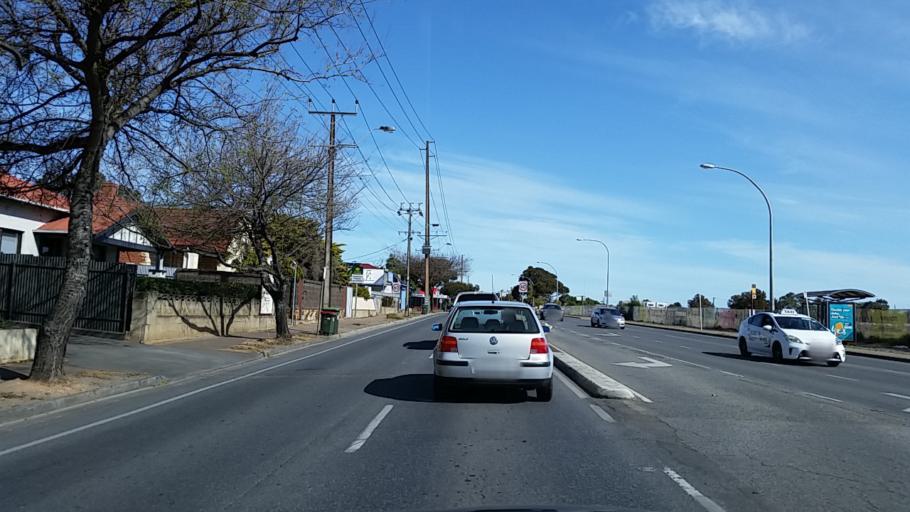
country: AU
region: South Australia
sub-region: Prospect
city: Prospect
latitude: -34.8751
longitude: 138.5842
